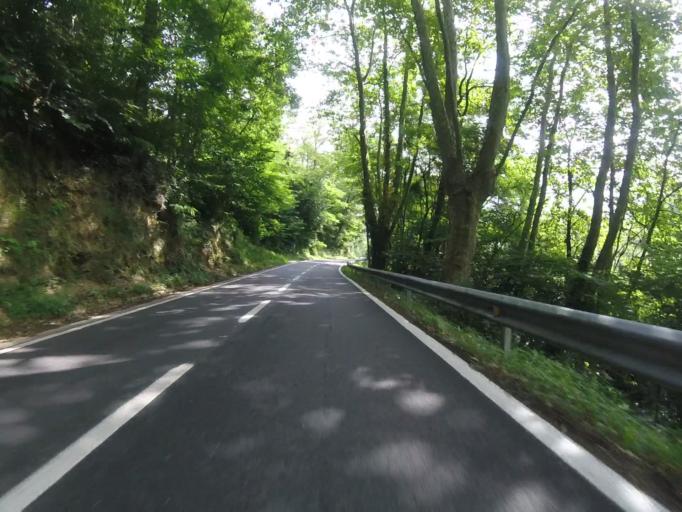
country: ES
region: Navarre
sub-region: Provincia de Navarra
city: Ituren
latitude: 43.1304
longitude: -1.7280
